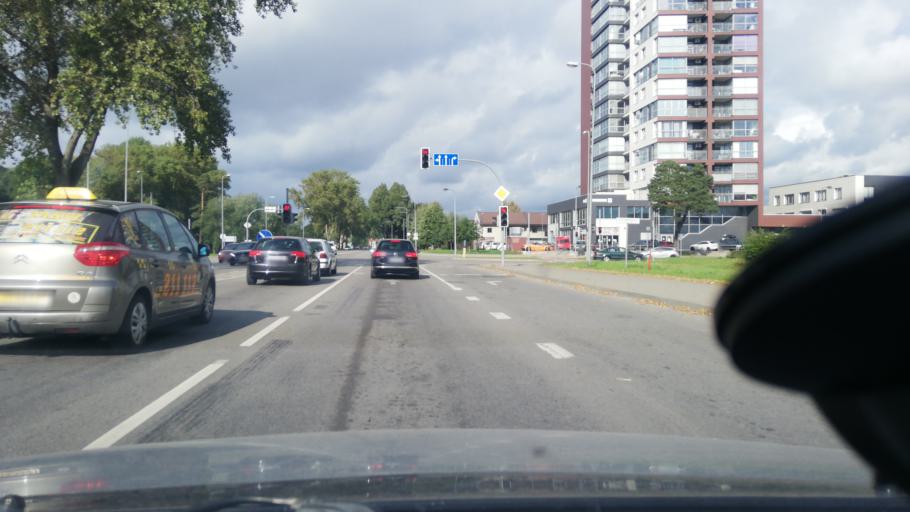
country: LT
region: Klaipedos apskritis
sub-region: Klaipeda
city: Klaipeda
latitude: 55.6703
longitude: 21.1591
